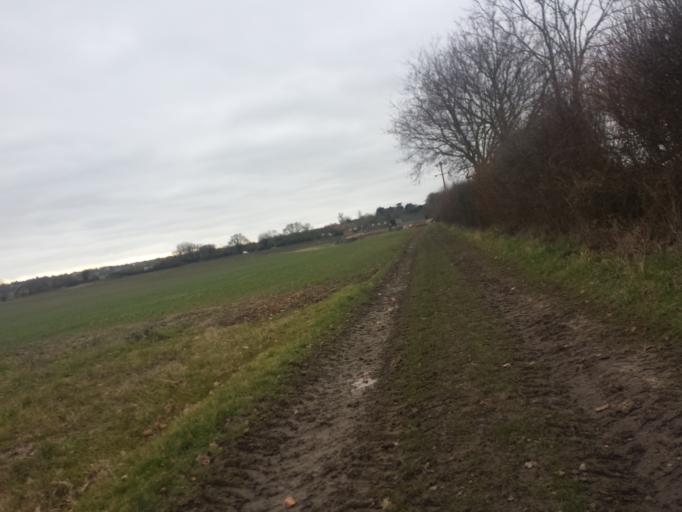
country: GB
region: England
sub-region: Essex
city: Little Clacton
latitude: 51.8831
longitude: 1.1712
